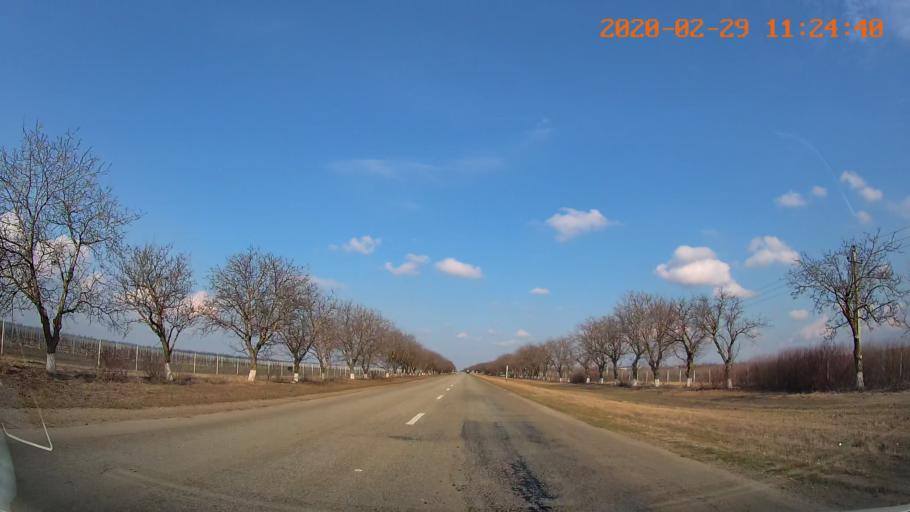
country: MD
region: Telenesti
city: Cocieri
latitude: 47.4272
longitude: 29.1536
